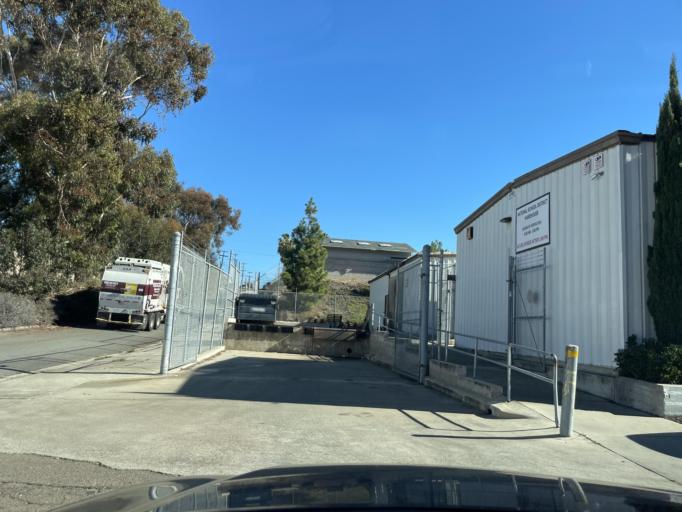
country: US
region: California
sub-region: San Diego County
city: National City
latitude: 32.6743
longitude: -117.0916
